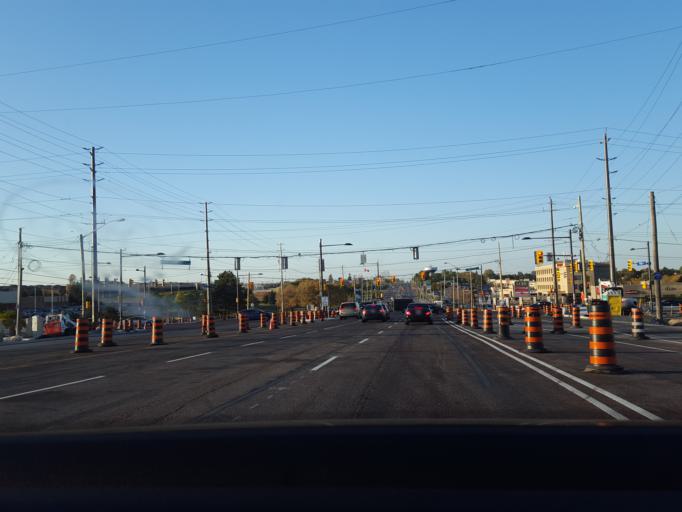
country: CA
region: Ontario
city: Newmarket
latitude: 44.0540
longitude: -79.4800
